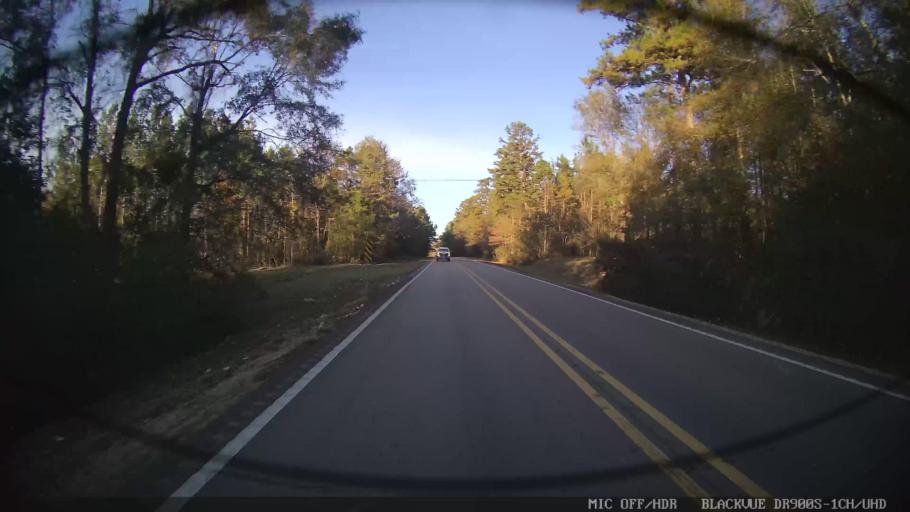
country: US
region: Mississippi
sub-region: Lamar County
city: Lumberton
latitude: 31.0613
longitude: -89.4258
